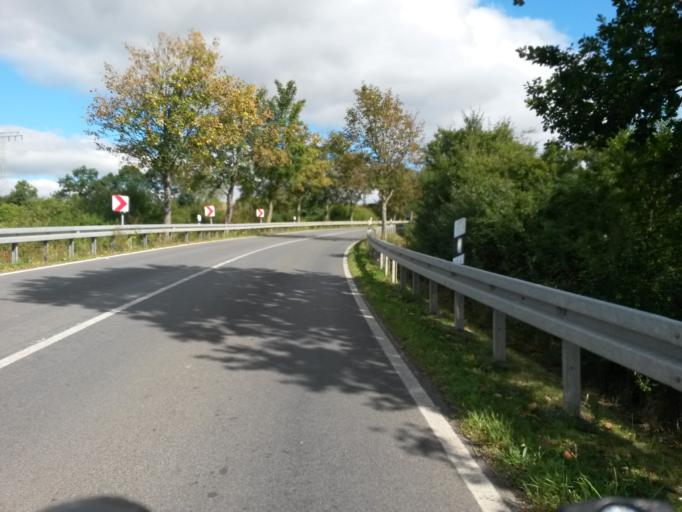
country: DE
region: Brandenburg
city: Mittenwalde
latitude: 53.2087
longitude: 13.5618
